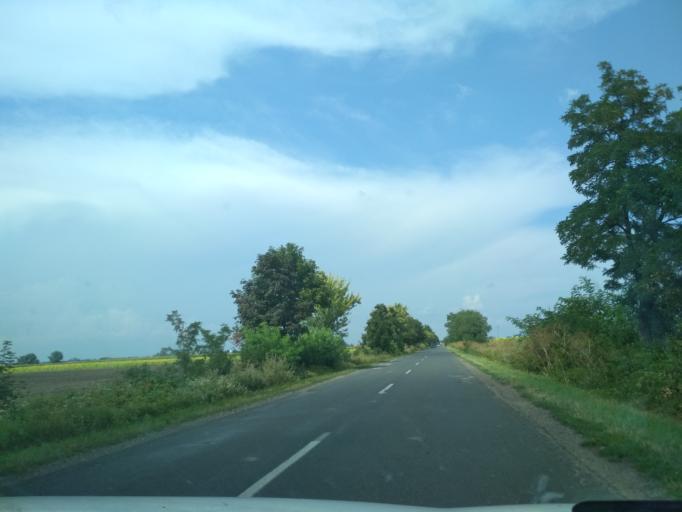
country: HU
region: Jasz-Nagykun-Szolnok
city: Tiszaszolos
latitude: 47.5381
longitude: 20.7164
